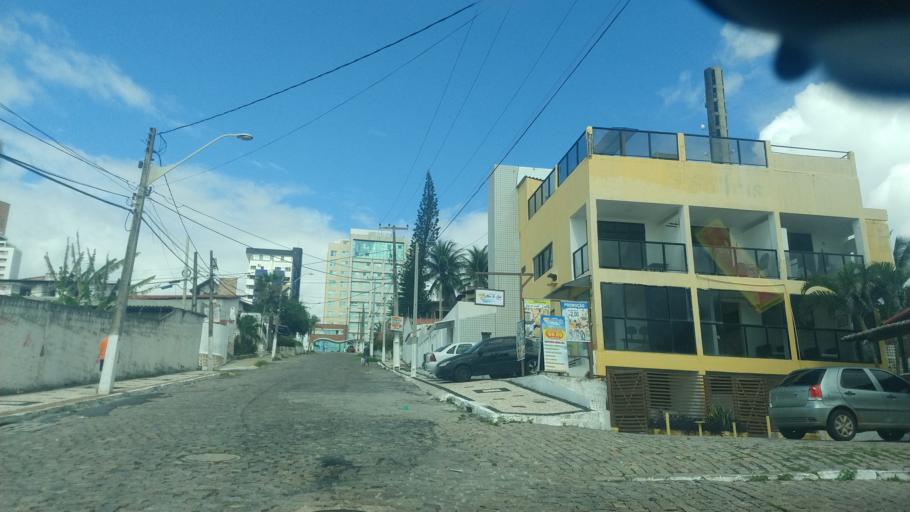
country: BR
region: Rio Grande do Norte
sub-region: Natal
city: Natal
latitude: -5.8717
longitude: -35.1789
